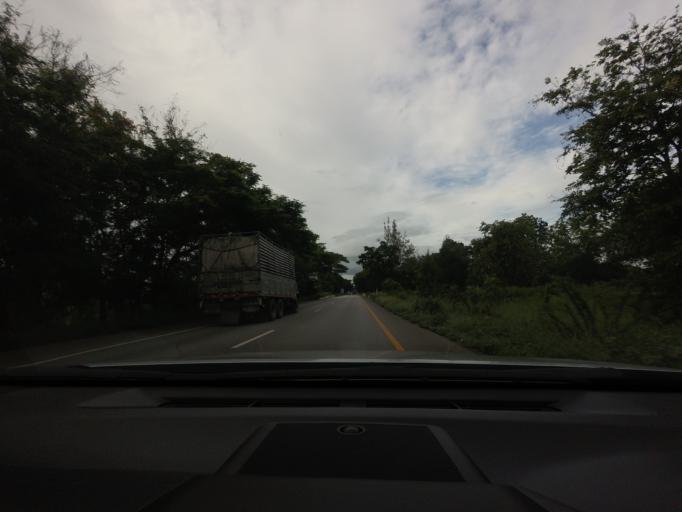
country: TH
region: Phetchaburi
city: Cha-am
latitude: 12.7113
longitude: 99.9149
